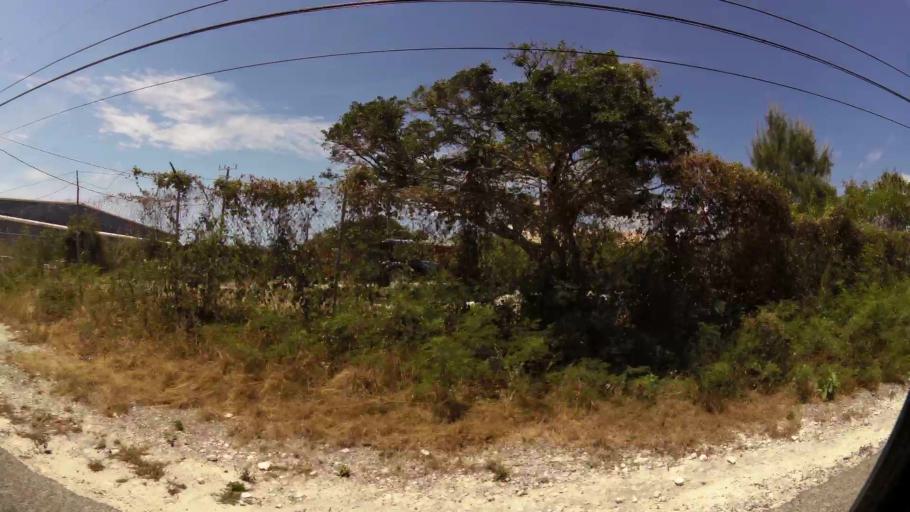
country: BS
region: Mayaguana
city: Abraham's Bay
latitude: 21.7760
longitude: -72.2623
